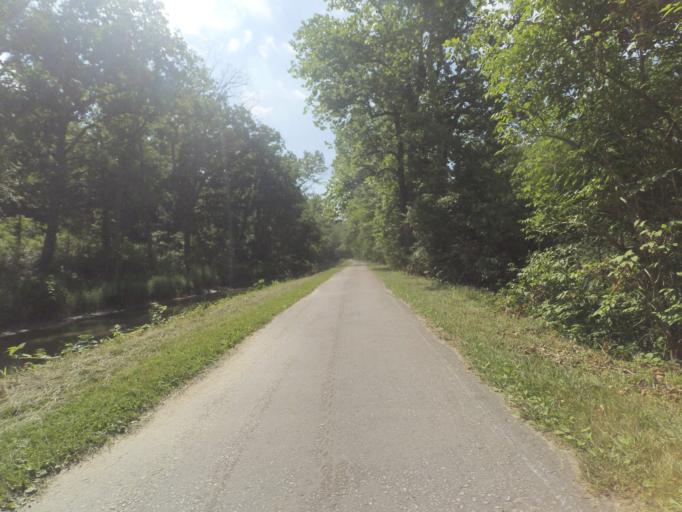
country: US
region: Ohio
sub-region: Cuyahoga County
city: Walton Hills
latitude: 41.3436
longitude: -81.5886
